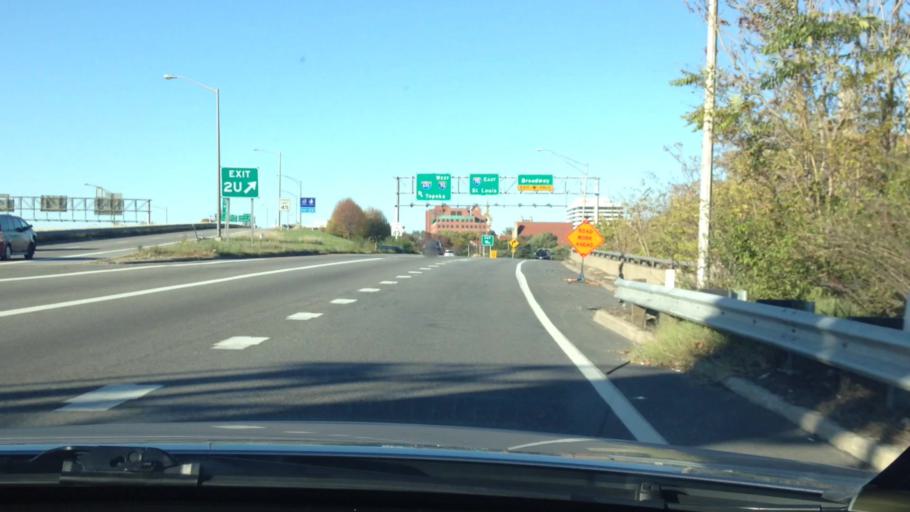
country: US
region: Missouri
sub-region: Jackson County
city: Kansas City
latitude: 39.0934
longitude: -94.5906
